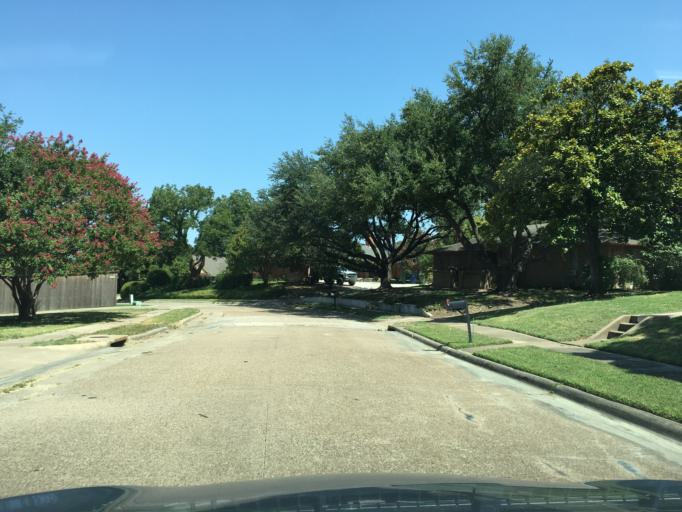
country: US
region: Texas
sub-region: Dallas County
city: Garland
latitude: 32.8752
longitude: -96.6069
